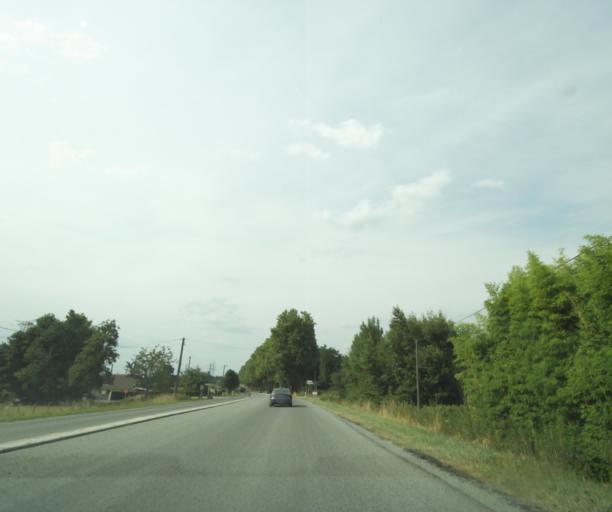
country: FR
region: Pays de la Loire
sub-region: Departement de la Sarthe
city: Teloche
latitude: 47.8710
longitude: 0.2526
